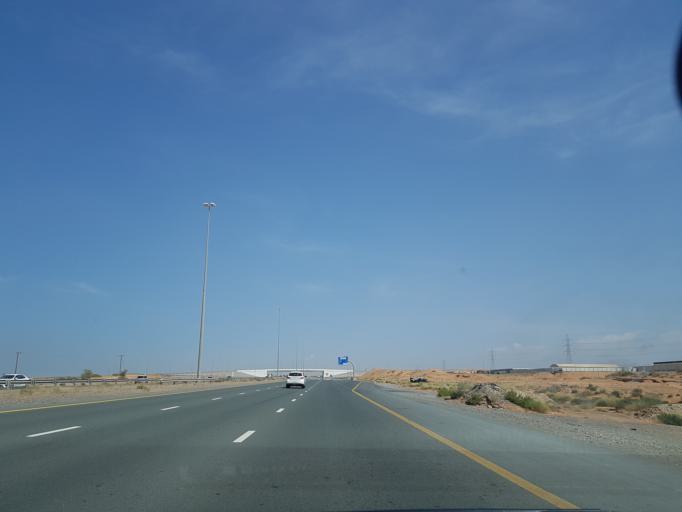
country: AE
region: Ra's al Khaymah
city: Ras al-Khaimah
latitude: 25.6671
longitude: 55.8767
